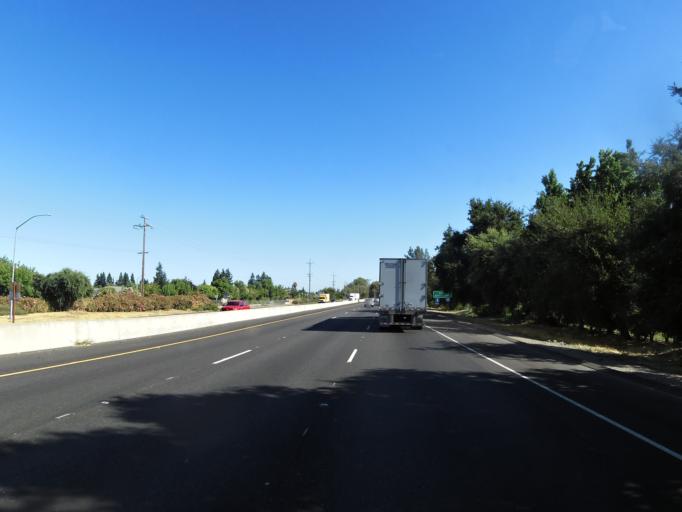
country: US
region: California
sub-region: San Joaquin County
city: Lodi
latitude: 38.1029
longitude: -121.2601
